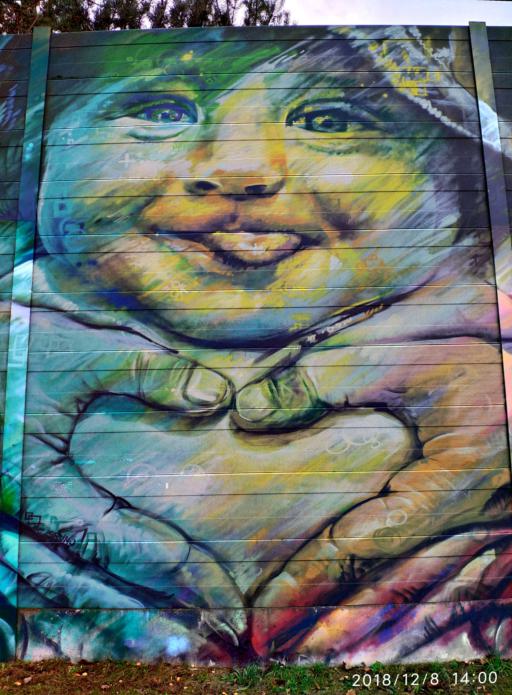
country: PL
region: Lubusz
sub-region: Zielona Gora
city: Zielona Gora
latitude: 51.9605
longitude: 15.5055
